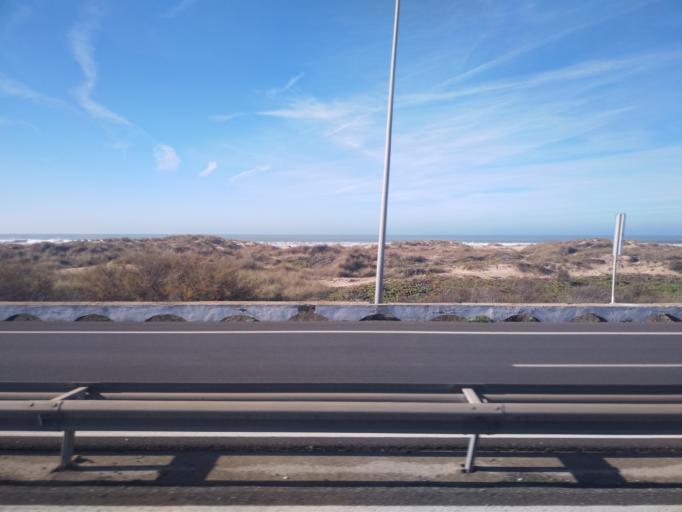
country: ES
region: Andalusia
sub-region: Provincia de Cadiz
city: San Fernando
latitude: 36.4660
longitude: -6.2537
